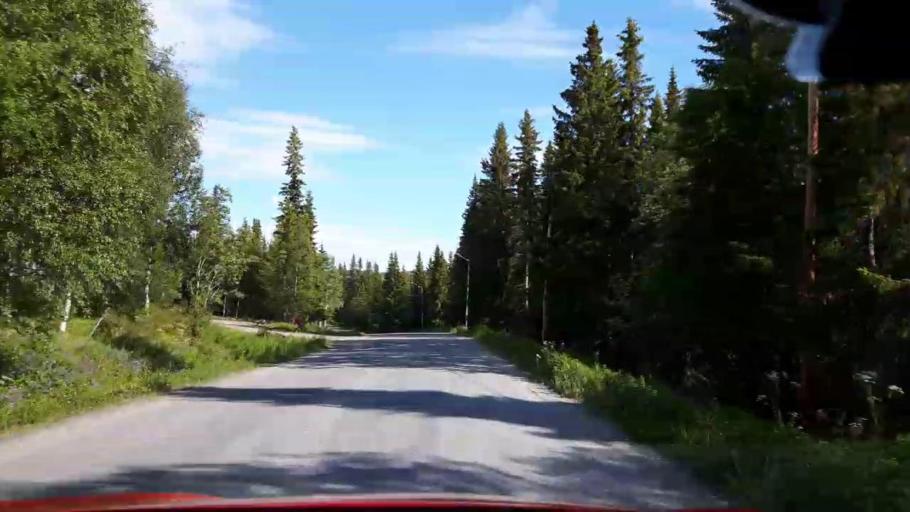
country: SE
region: Jaemtland
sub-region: Krokoms Kommun
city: Valla
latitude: 63.7635
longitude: 14.0843
